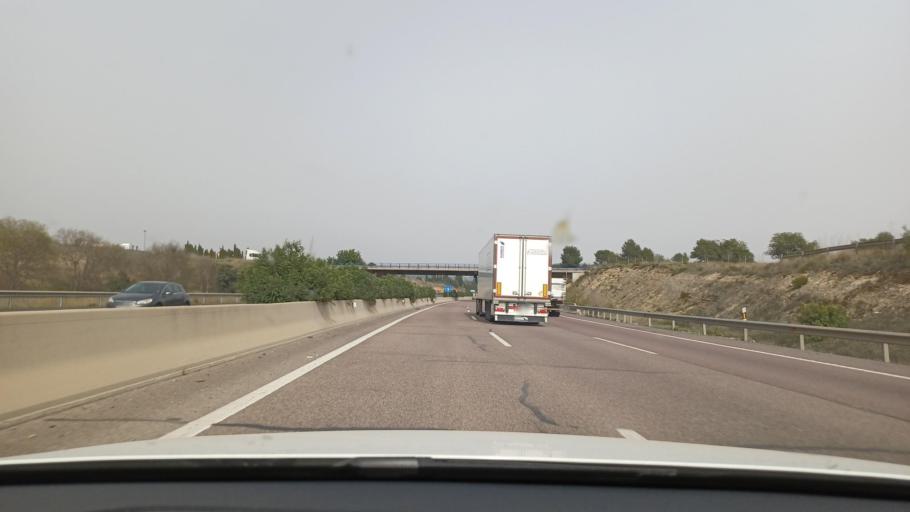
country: ES
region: Valencia
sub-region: Provincia de Valencia
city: Manises
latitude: 39.5043
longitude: -0.5193
